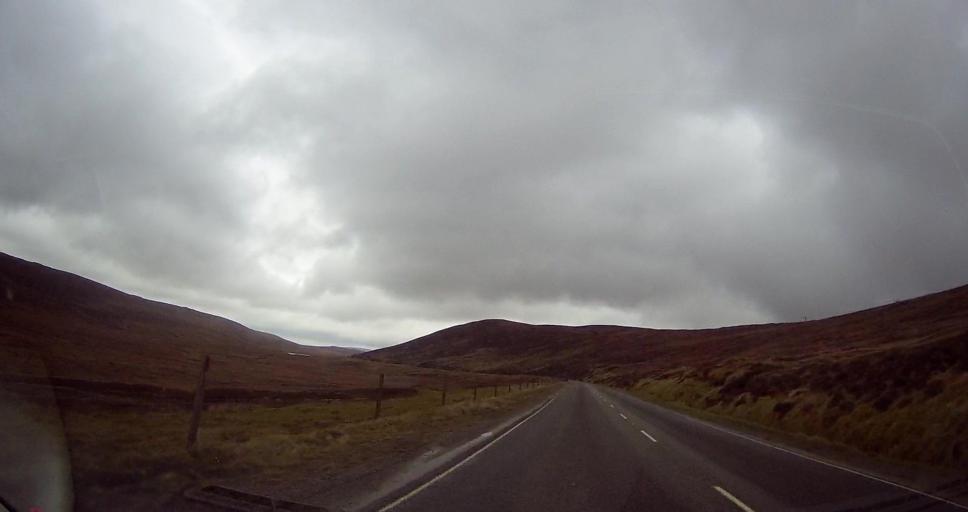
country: GB
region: Scotland
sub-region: Shetland Islands
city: Lerwick
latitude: 60.2984
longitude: -1.2393
